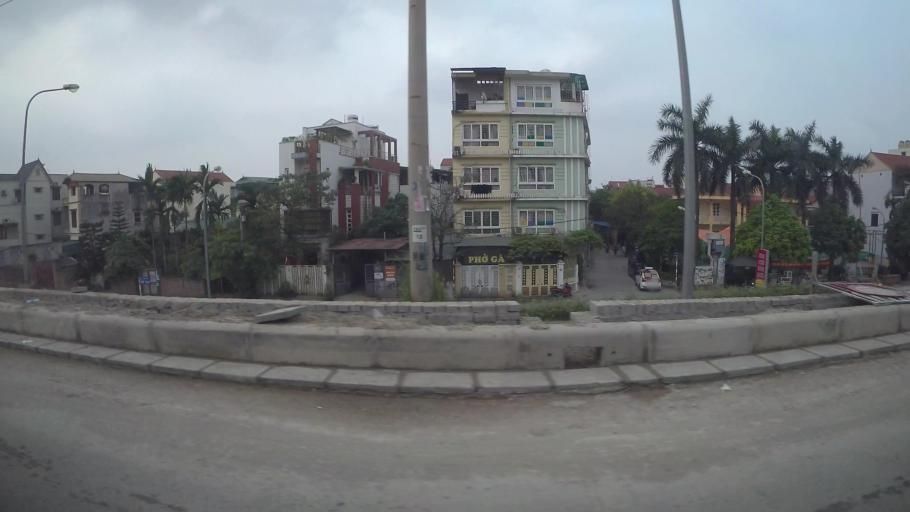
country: VN
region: Ha Noi
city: Trau Quy
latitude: 21.0213
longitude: 105.8985
